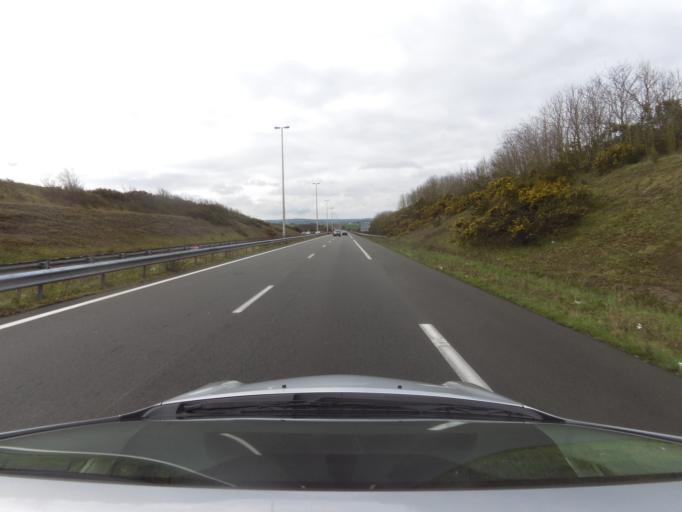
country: FR
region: Nord-Pas-de-Calais
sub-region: Departement du Pas-de-Calais
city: Marquise
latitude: 50.8390
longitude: 1.7081
